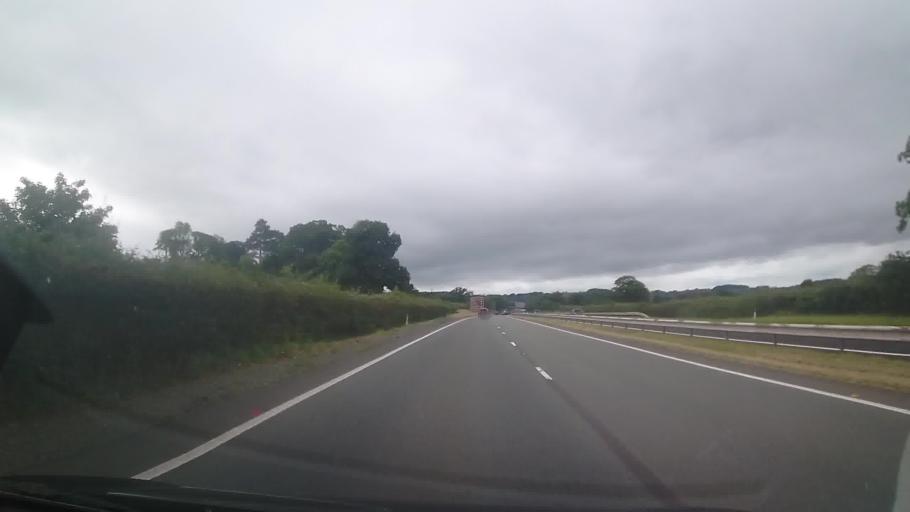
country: GB
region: Wales
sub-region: Gwynedd
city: Bethesda
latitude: 53.2143
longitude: -4.0771
